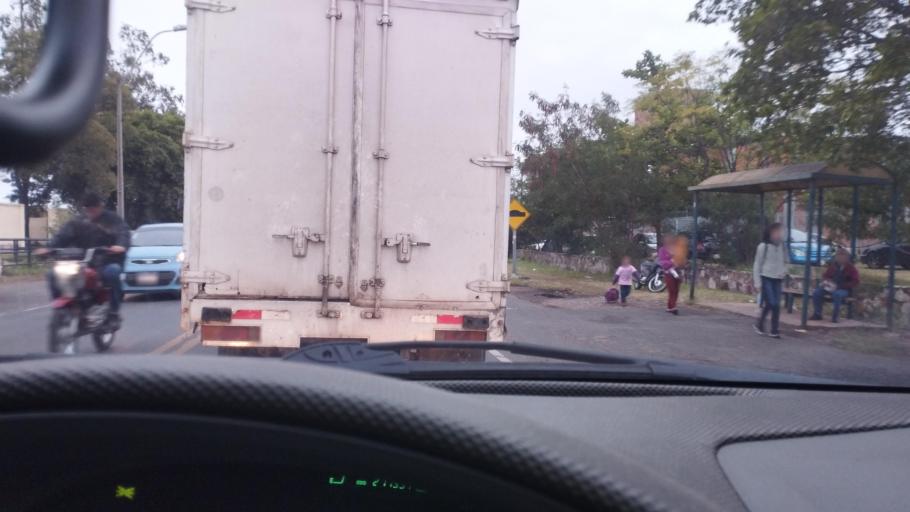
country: PY
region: Central
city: Fernando de la Mora
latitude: -25.2709
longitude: -57.5221
